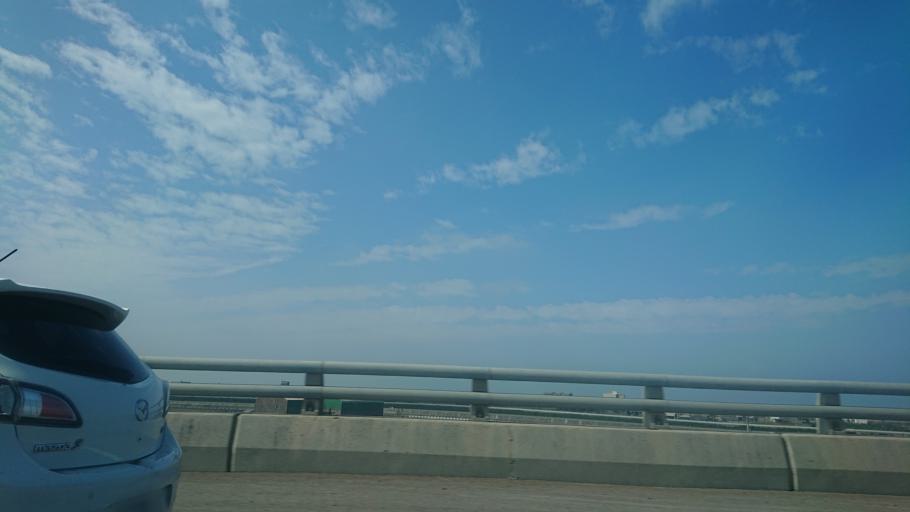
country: TW
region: Taiwan
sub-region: Changhua
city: Chang-hua
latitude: 24.0490
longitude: 120.4060
